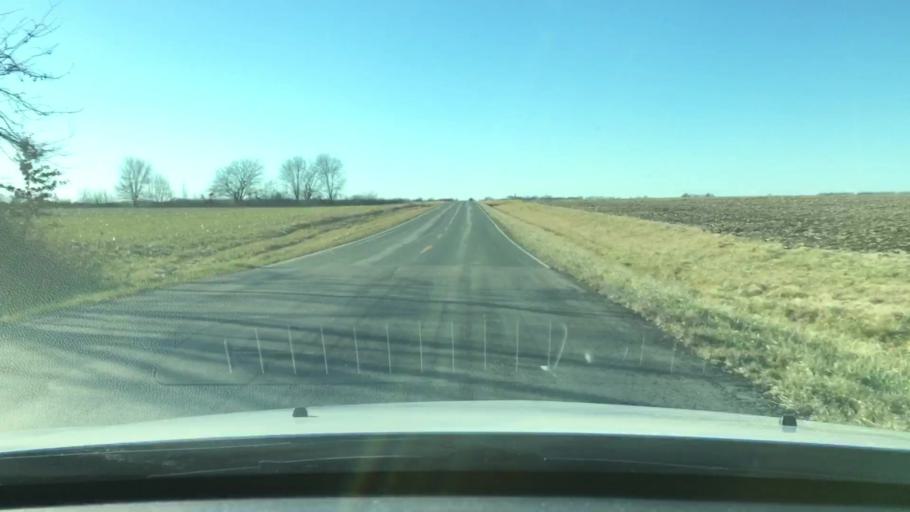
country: US
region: Missouri
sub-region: Audrain County
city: Vandalia
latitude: 39.2814
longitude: -91.6897
